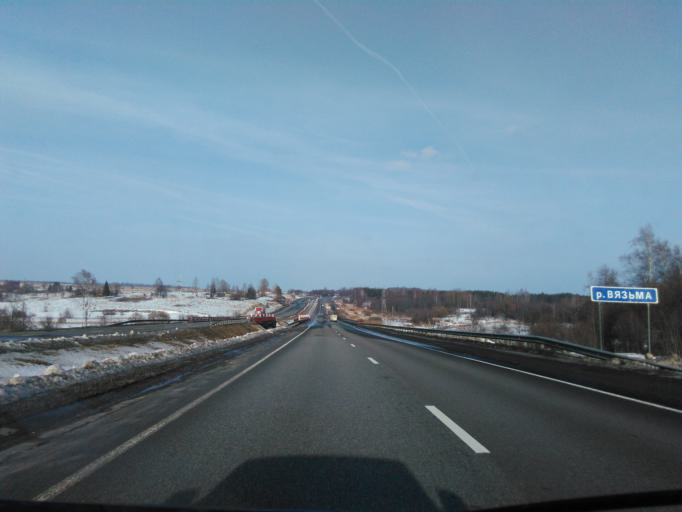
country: RU
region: Smolensk
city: Vyaz'ma
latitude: 55.2050
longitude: 34.1477
